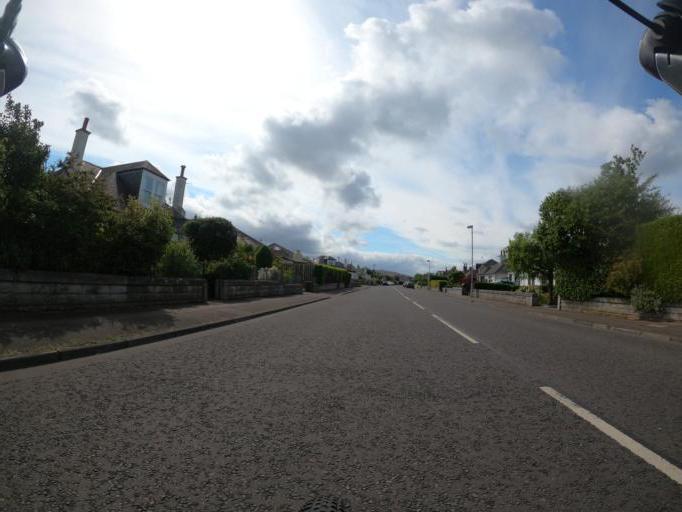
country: GB
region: Scotland
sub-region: East Lothian
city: Musselburgh
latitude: 55.9470
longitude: -3.0921
